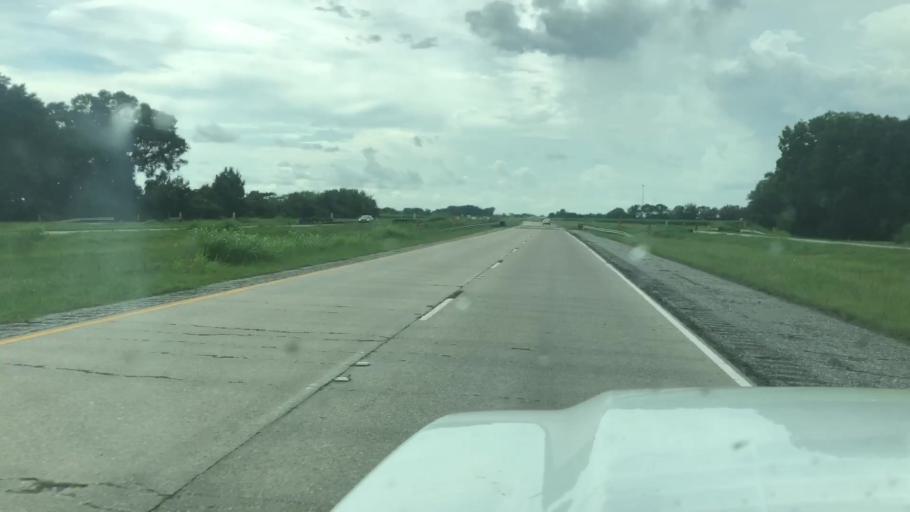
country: US
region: Louisiana
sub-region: Saint Mary Parish
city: Baldwin
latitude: 29.8568
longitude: -91.6107
